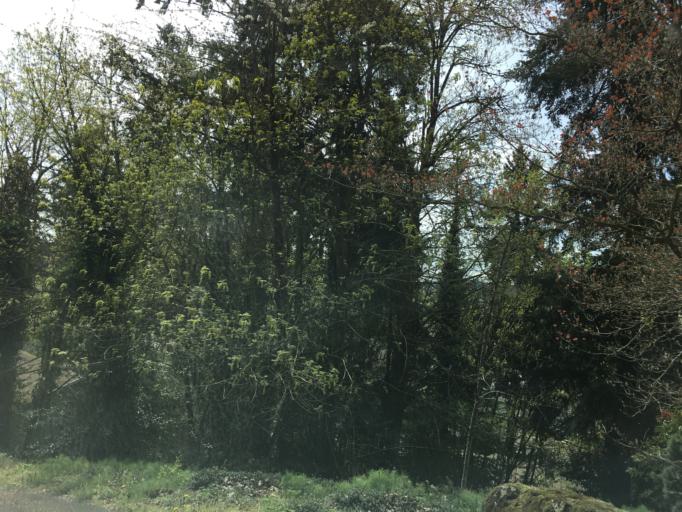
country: US
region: Oregon
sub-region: Multnomah County
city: Lents
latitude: 45.5405
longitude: -122.5675
